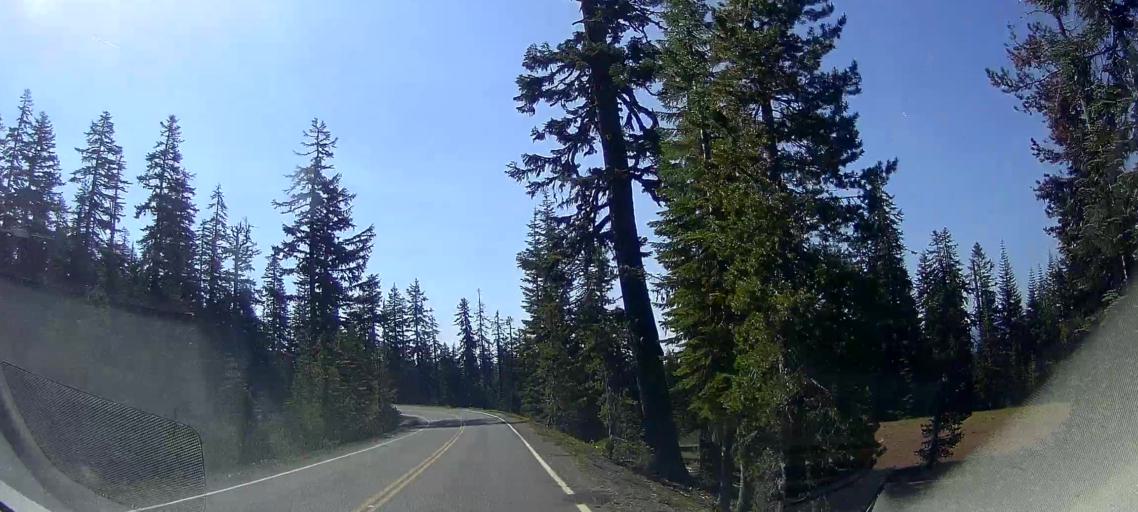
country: US
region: Oregon
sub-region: Klamath County
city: Klamath Falls
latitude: 42.8771
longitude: -122.1073
